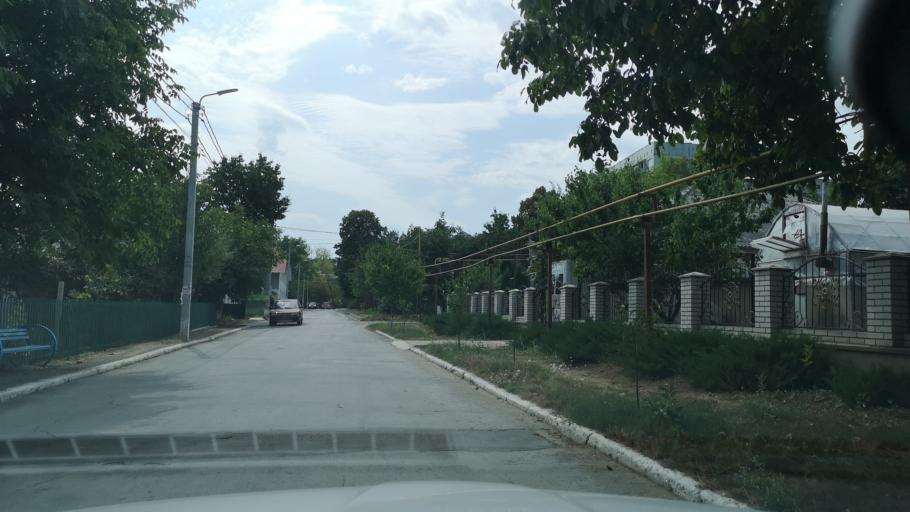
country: MD
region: Rezina
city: Rezina
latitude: 47.7508
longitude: 28.9587
